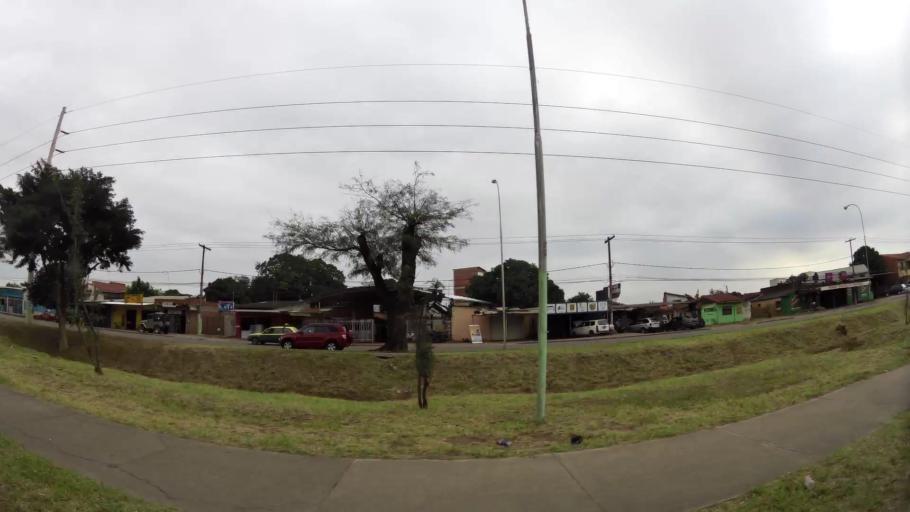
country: BO
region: Santa Cruz
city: Santa Cruz de la Sierra
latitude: -17.8030
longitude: -63.1518
